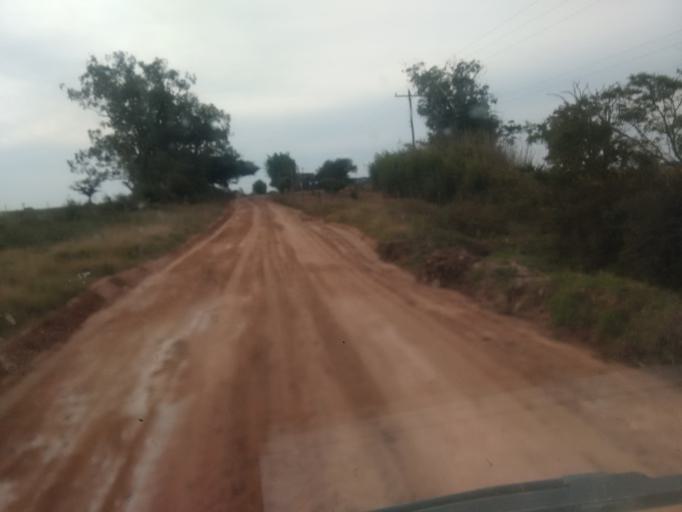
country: BR
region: Rio Grande do Sul
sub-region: Sao Lourenco Do Sul
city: Sao Lourenco do Sul
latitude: -31.1554
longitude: -51.7558
